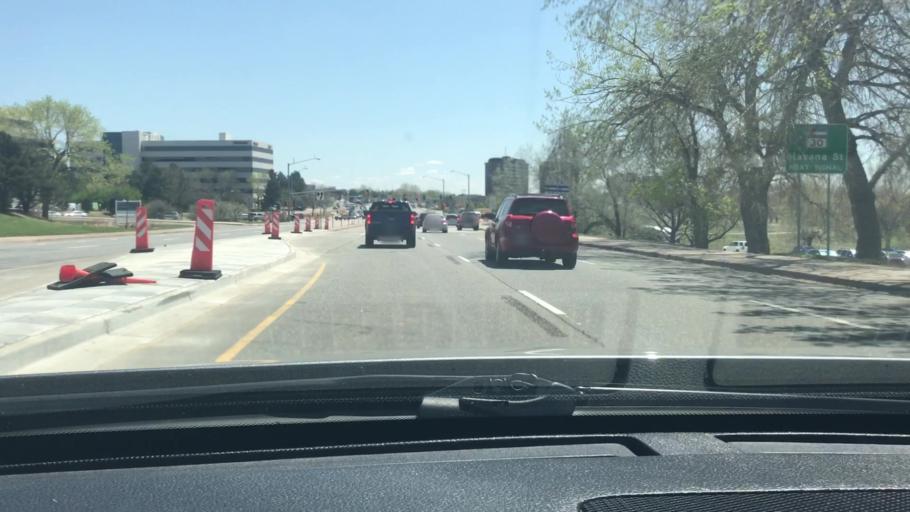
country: US
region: Colorado
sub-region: Adams County
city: Aurora
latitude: 39.6722
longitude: -104.8678
